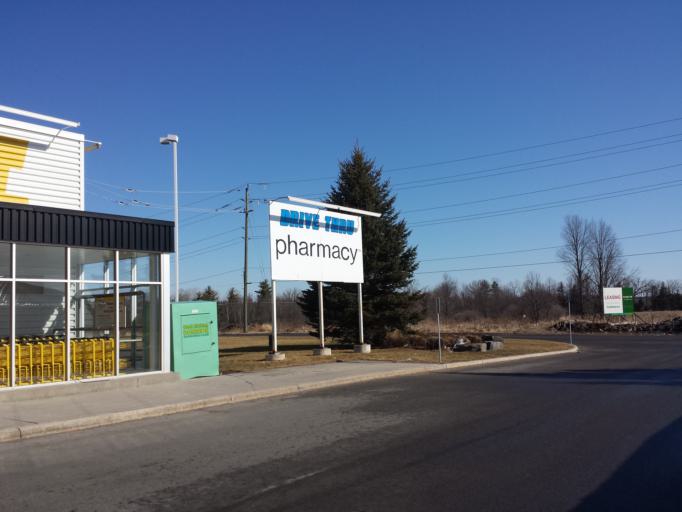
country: CA
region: Ontario
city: Renfrew
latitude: 45.4769
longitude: -76.6599
